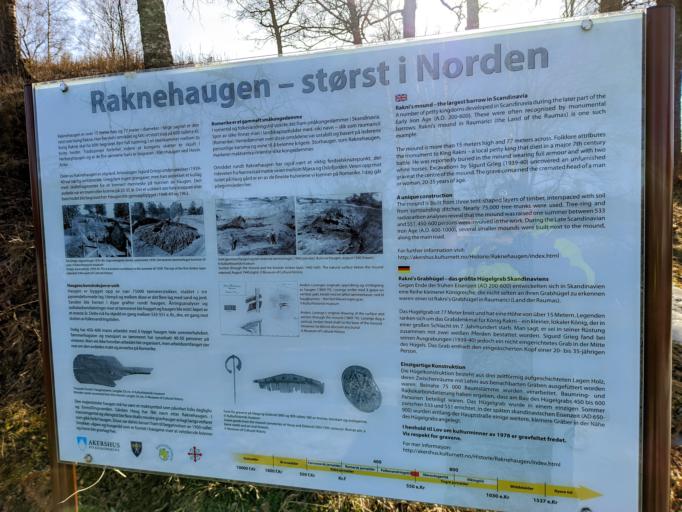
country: NO
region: Akershus
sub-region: Ullensaker
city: Jessheim
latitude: 60.1474
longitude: 11.1369
